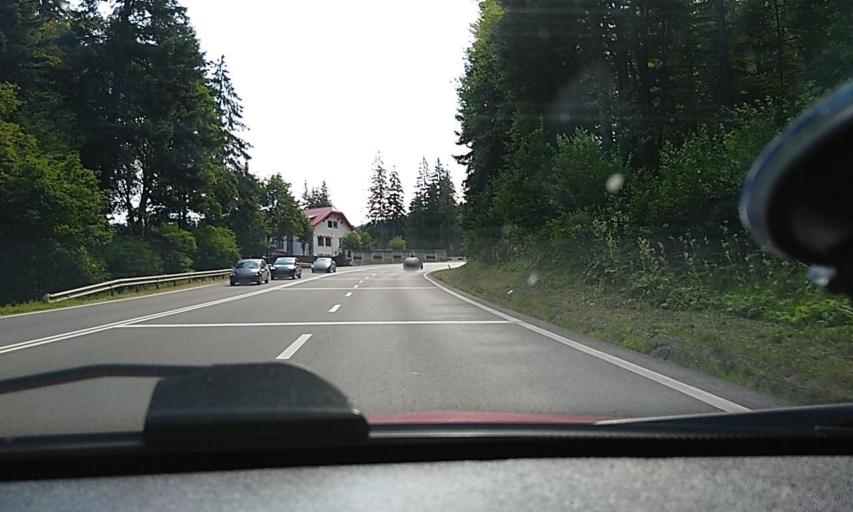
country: RO
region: Brasov
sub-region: Oras Predeal
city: Predeal
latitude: 45.5257
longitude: 25.5771
